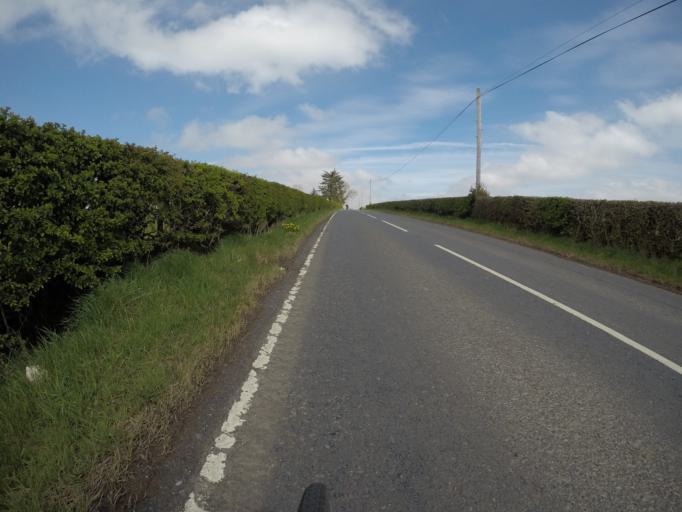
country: GB
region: Scotland
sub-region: East Ayrshire
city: Stewarton
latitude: 55.6910
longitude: -4.4953
